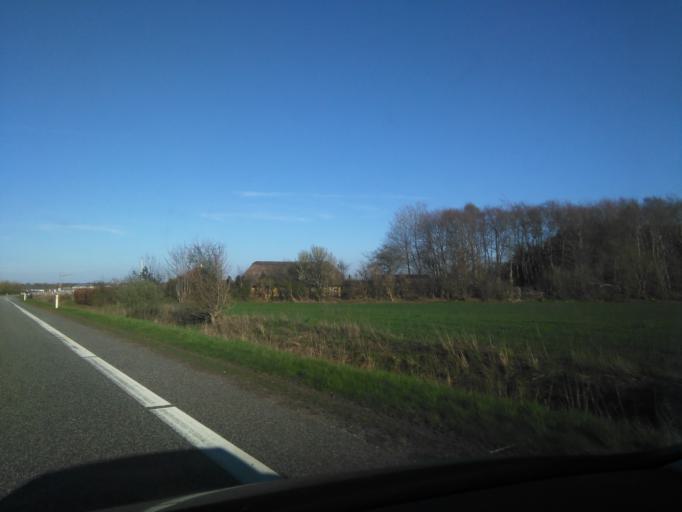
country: DK
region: Central Jutland
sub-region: Herning Kommune
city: Snejbjerg
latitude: 56.1276
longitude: 8.8627
